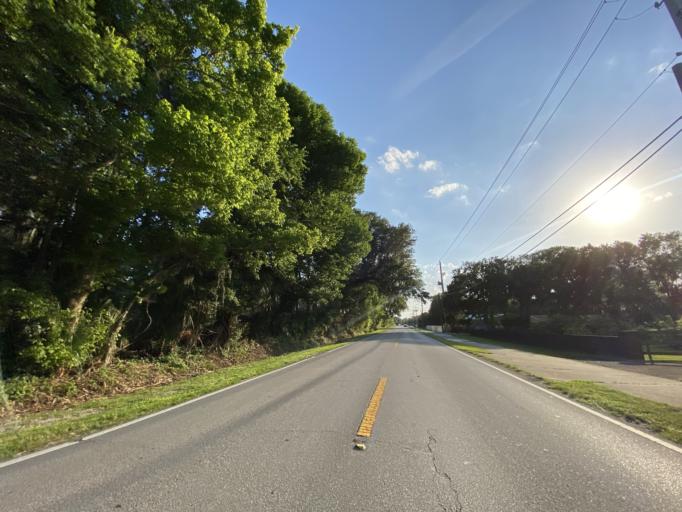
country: US
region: Florida
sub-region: Volusia County
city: Port Orange
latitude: 29.1458
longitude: -81.0114
